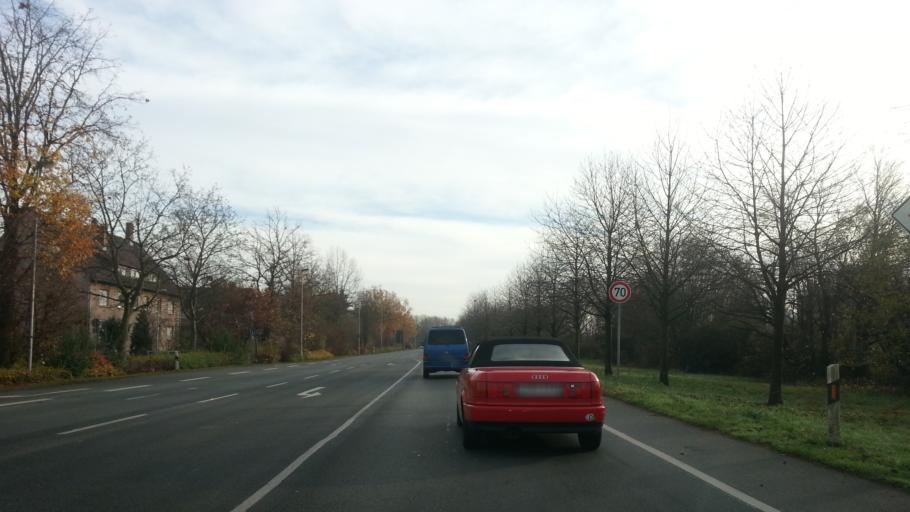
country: DE
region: Hesse
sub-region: Regierungsbezirk Darmstadt
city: Gross-Gerau
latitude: 49.9150
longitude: 8.4798
